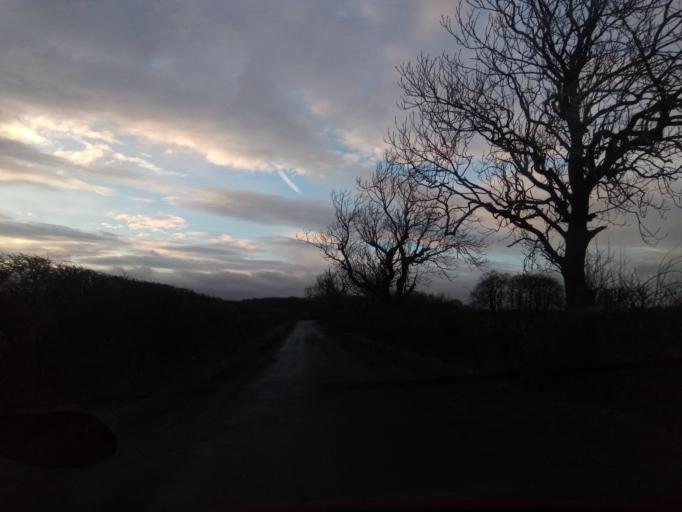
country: GB
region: England
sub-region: Northumberland
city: Ponteland
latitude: 55.0836
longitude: -1.7544
